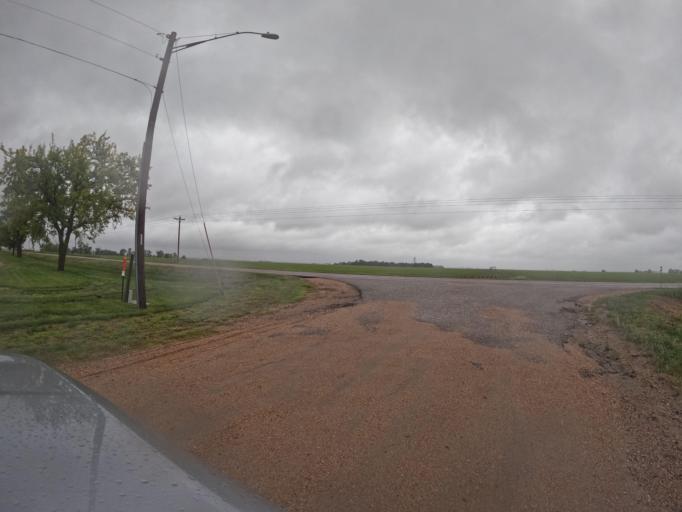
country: US
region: Nebraska
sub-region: Clay County
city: Harvard
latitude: 40.6116
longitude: -98.0945
